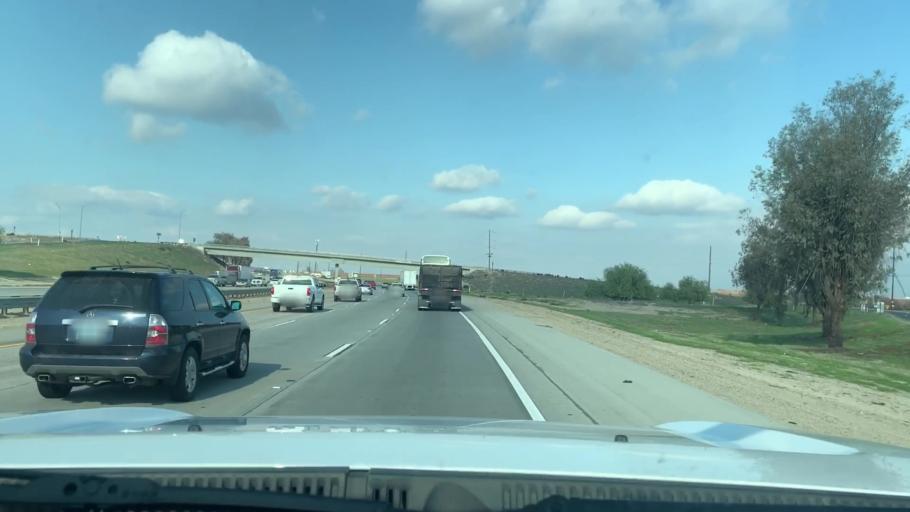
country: US
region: California
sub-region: Kern County
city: Shafter
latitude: 35.5565
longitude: -119.1969
